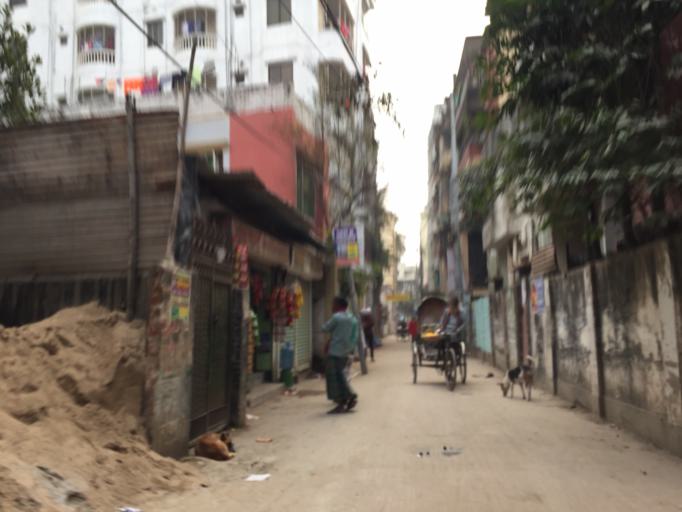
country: BD
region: Dhaka
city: Azimpur
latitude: 23.7946
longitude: 90.3618
